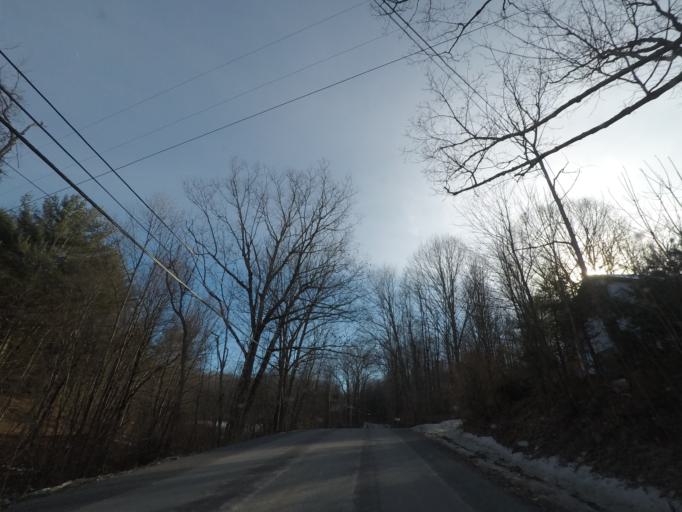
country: US
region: New York
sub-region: Rensselaer County
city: Hoosick Falls
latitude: 42.7603
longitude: -73.3616
